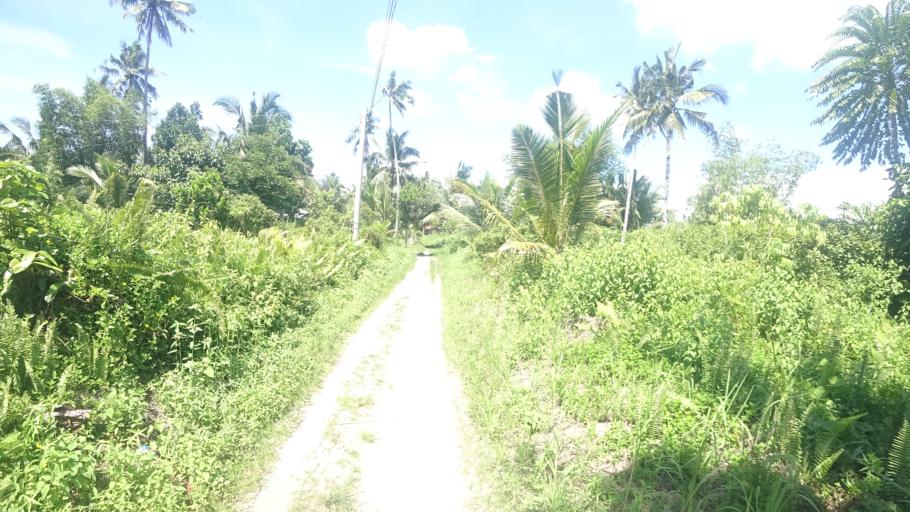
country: PH
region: Eastern Visayas
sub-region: Province of Leyte
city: Liberty
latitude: 10.8838
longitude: 125.0059
